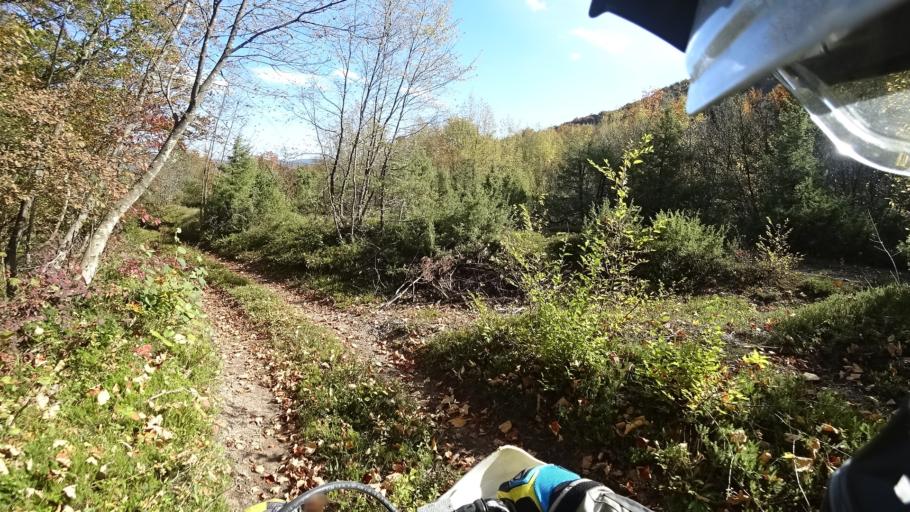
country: HR
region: Karlovacka
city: Plaski
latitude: 45.0817
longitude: 15.3224
